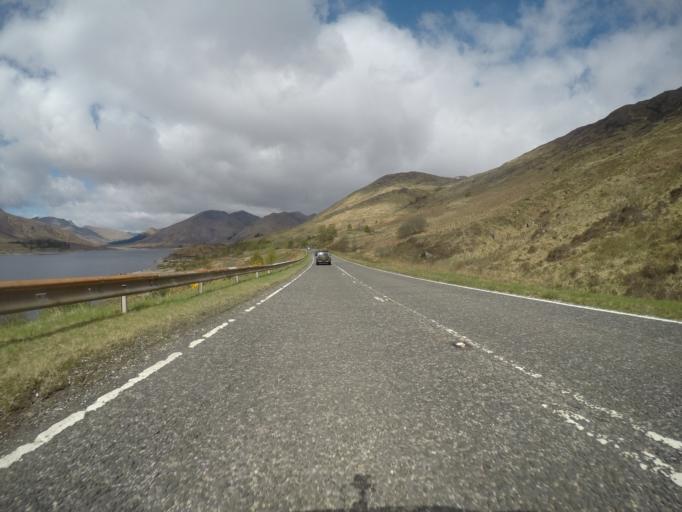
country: GB
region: Scotland
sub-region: Highland
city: Spean Bridge
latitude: 57.1518
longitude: -5.1249
